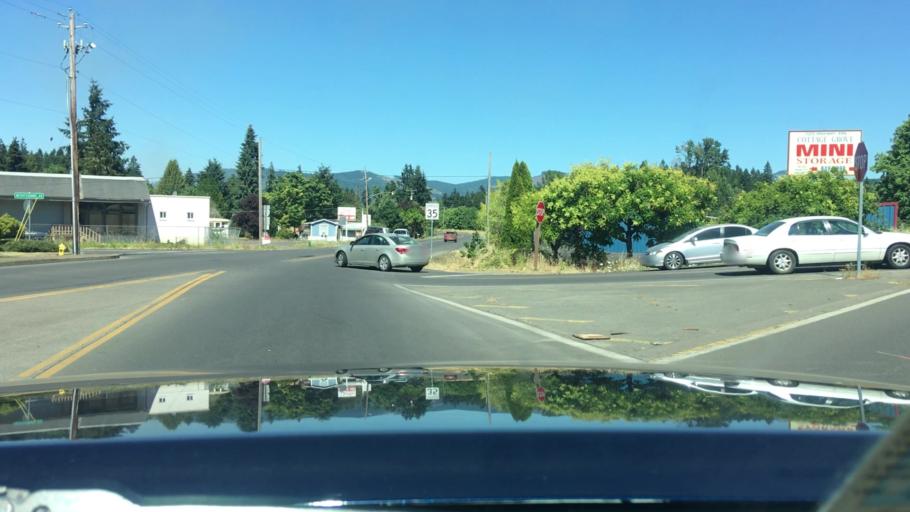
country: US
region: Oregon
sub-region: Lane County
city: Cottage Grove
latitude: 43.8055
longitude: -123.0544
